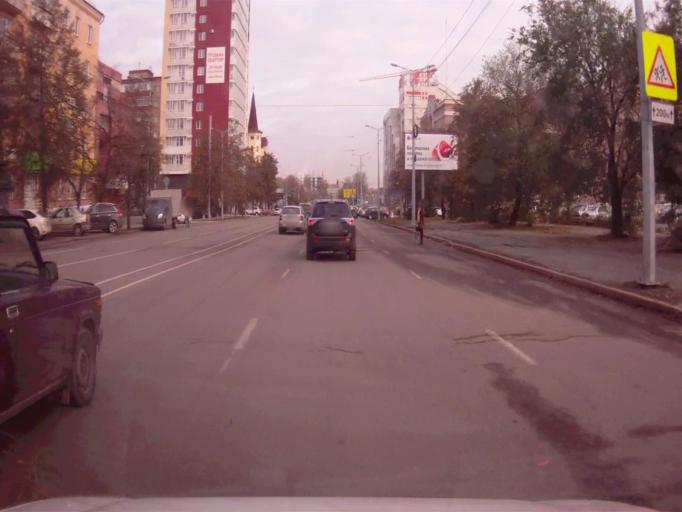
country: RU
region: Chelyabinsk
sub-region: Gorod Chelyabinsk
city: Chelyabinsk
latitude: 55.1712
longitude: 61.4118
